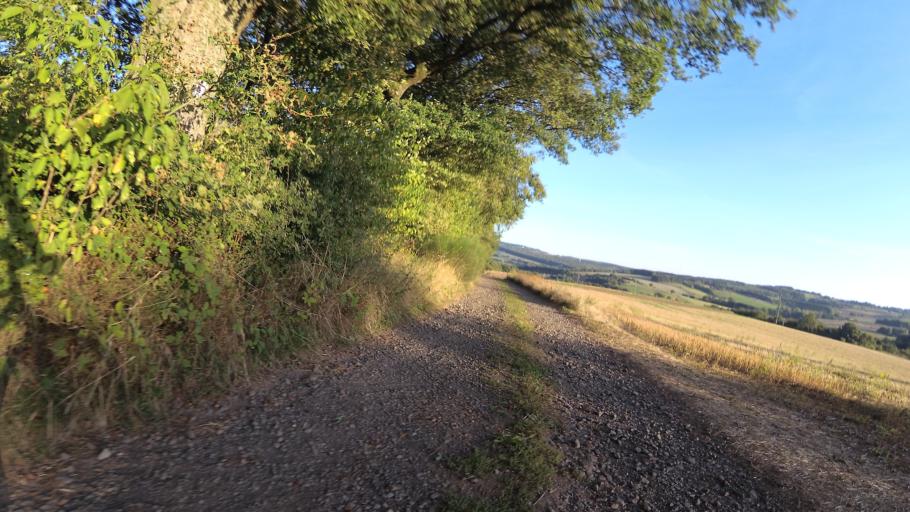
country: DE
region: Rheinland-Pfalz
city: Breitenbach
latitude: 49.4339
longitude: 7.2205
